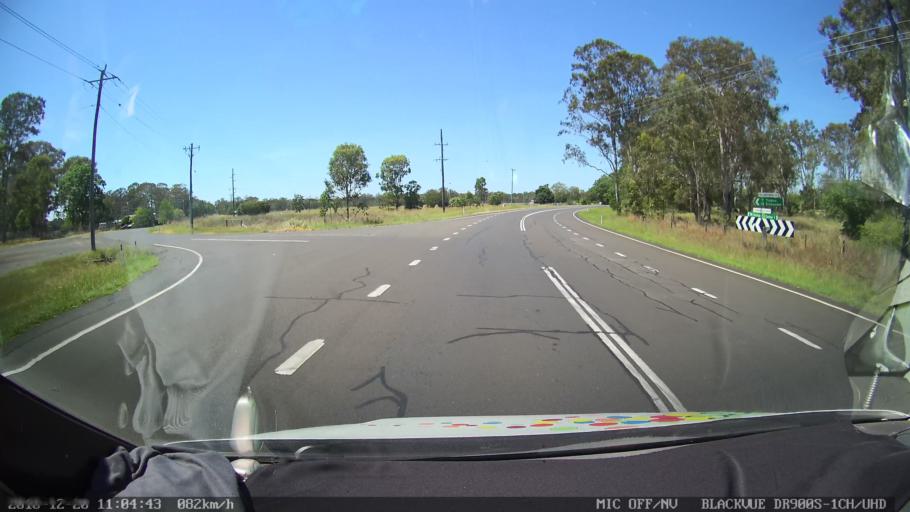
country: AU
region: New South Wales
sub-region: Richmond Valley
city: Casino
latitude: -28.8884
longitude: 153.0465
